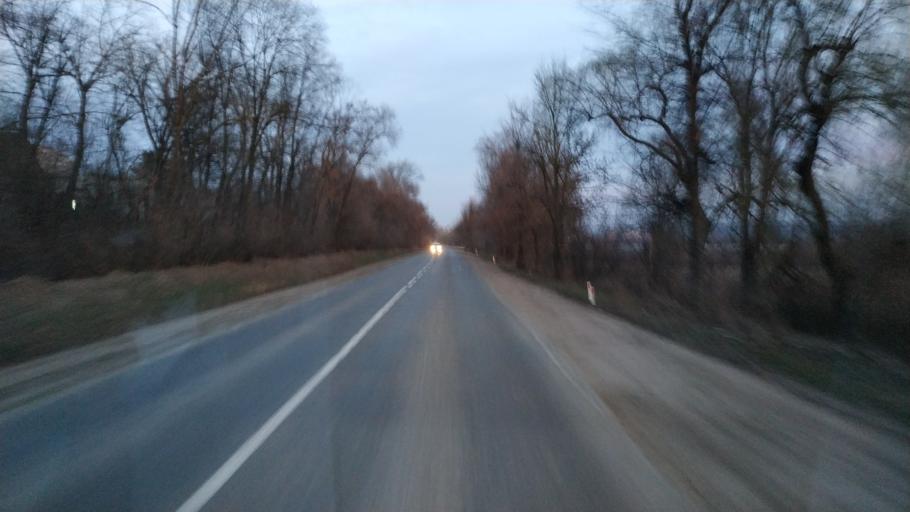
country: MD
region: Laloveni
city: Ialoveni
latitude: 46.9555
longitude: 28.7522
